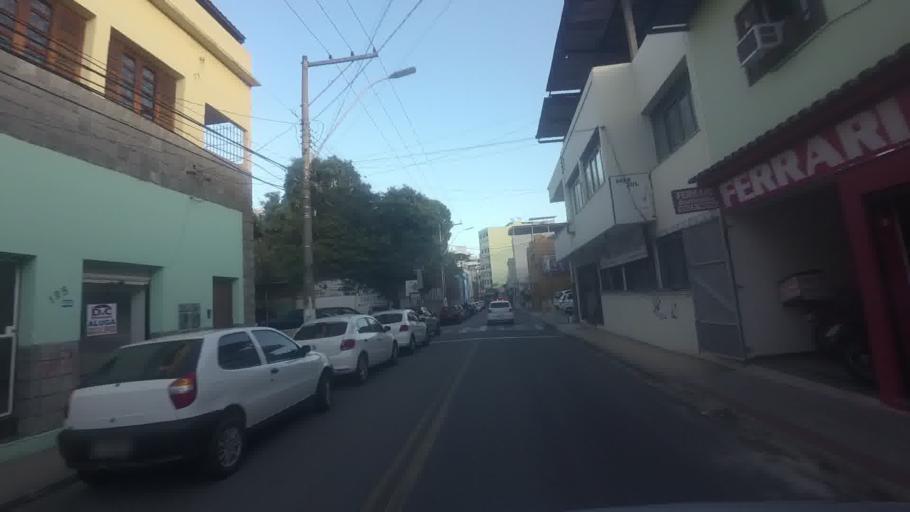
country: BR
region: Espirito Santo
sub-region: Cachoeiro De Itapemirim
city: Cachoeiro de Itapemirim
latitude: -20.8482
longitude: -41.1106
